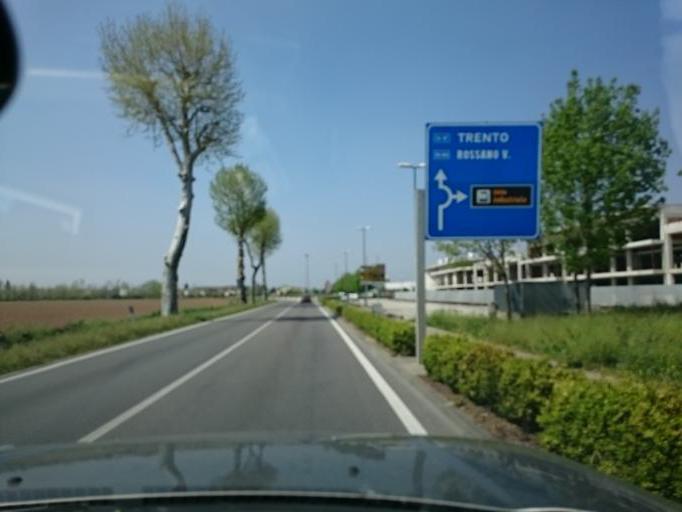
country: IT
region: Veneto
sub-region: Provincia di Vicenza
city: Rossano Veneto
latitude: 45.6997
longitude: 11.8263
